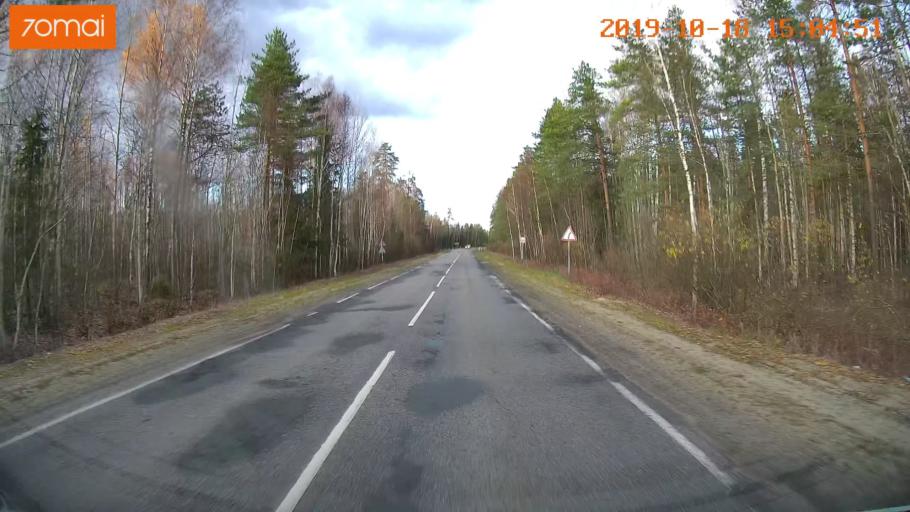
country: RU
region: Vladimir
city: Kurlovo
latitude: 55.5069
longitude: 40.5706
